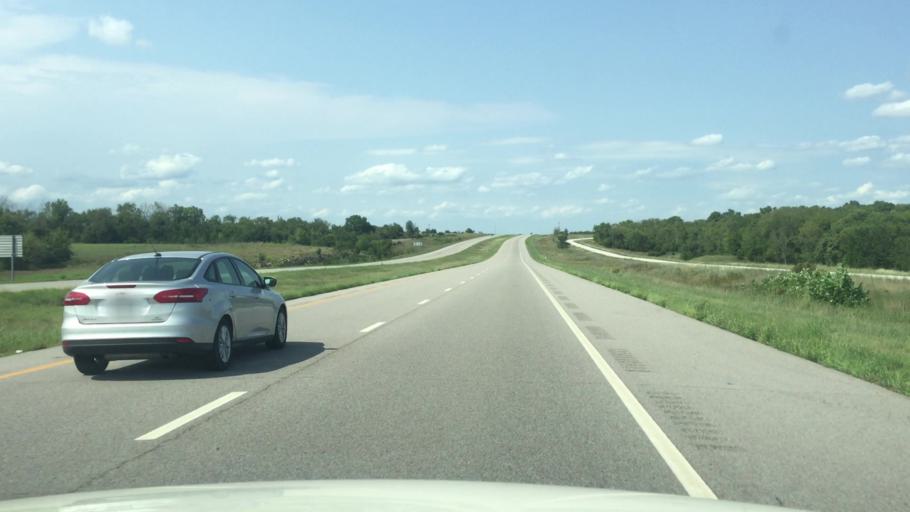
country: US
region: Kansas
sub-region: Linn County
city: La Cygne
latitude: 38.4118
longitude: -94.6876
